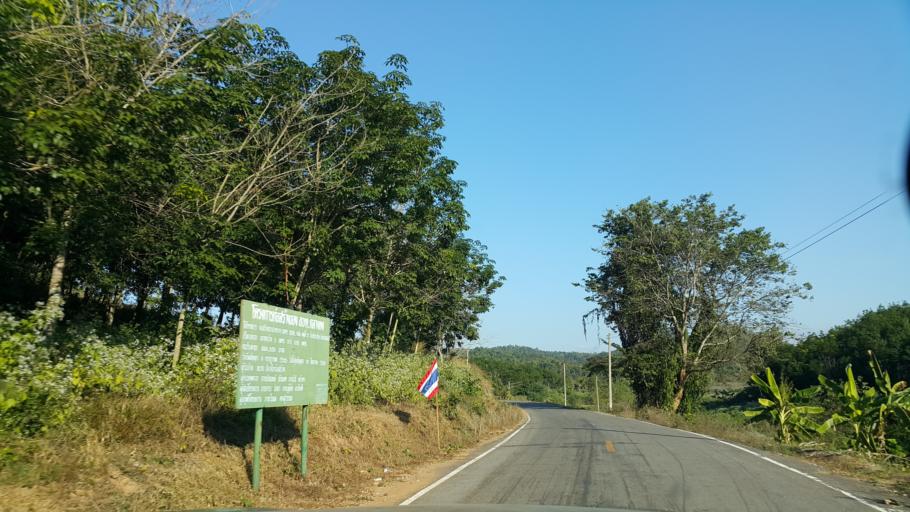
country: TH
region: Sukhothai
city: Thung Saliam
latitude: 17.4009
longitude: 99.5109
